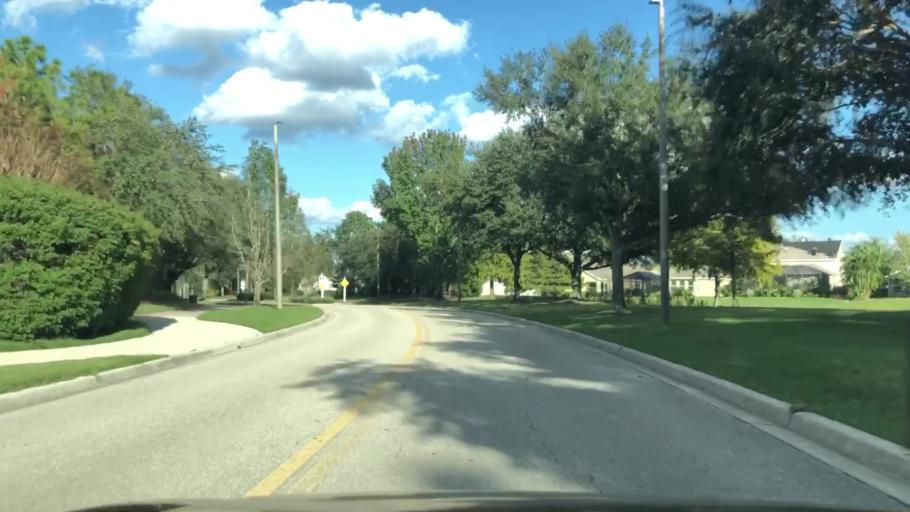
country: US
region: Florida
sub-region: Sarasota County
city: The Meadows
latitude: 27.4283
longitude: -82.4052
